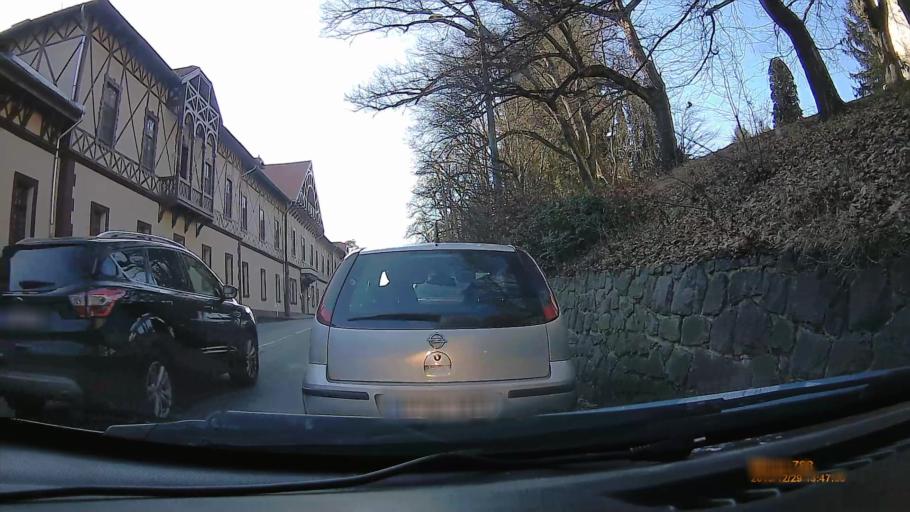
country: HU
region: Heves
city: Parad
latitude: 47.9259
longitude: 20.0606
